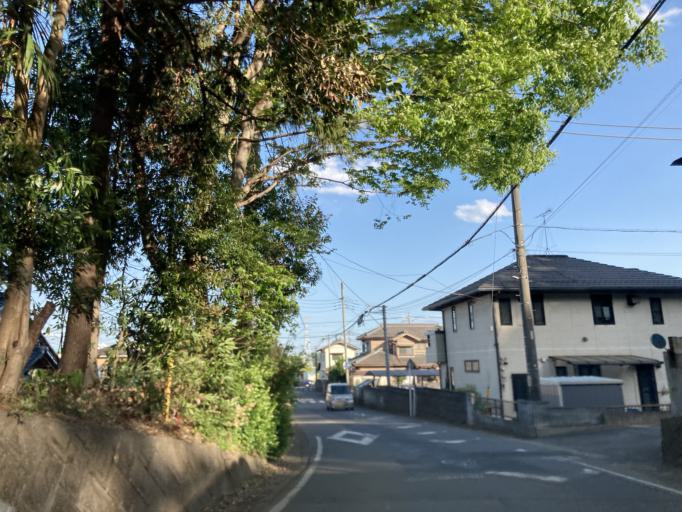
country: JP
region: Saitama
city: Sayama
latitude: 35.8553
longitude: 139.4432
